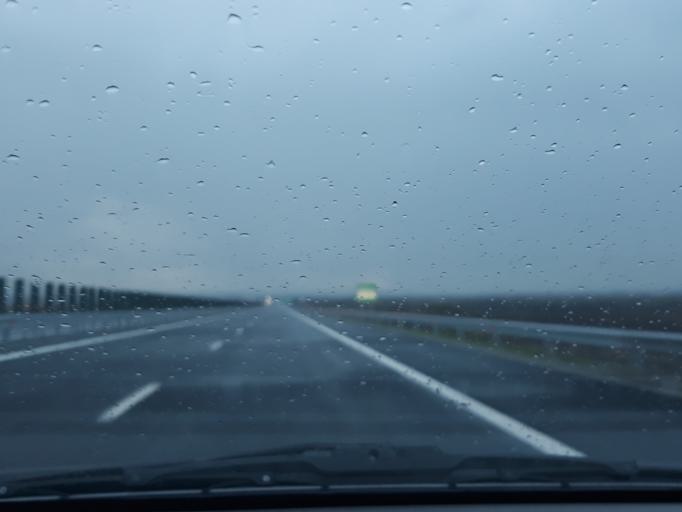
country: RO
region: Mures
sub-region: Comuna Ogra
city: Ogra
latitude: 46.4369
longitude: 24.3189
